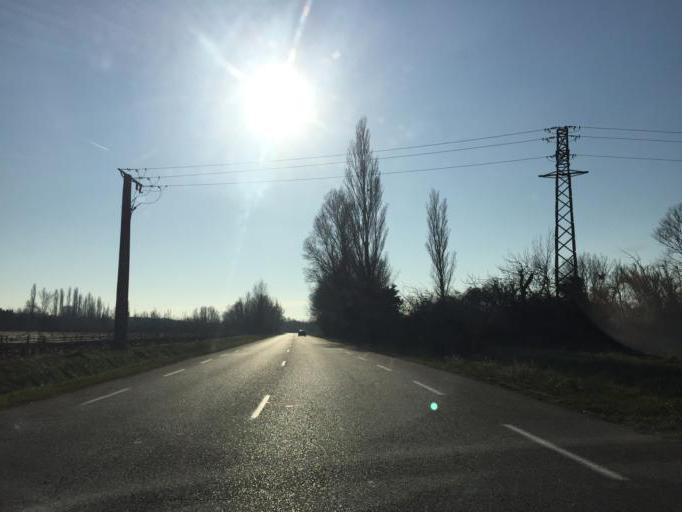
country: FR
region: Provence-Alpes-Cote d'Azur
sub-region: Departement du Vaucluse
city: Bedarrides
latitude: 44.0299
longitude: 4.8833
